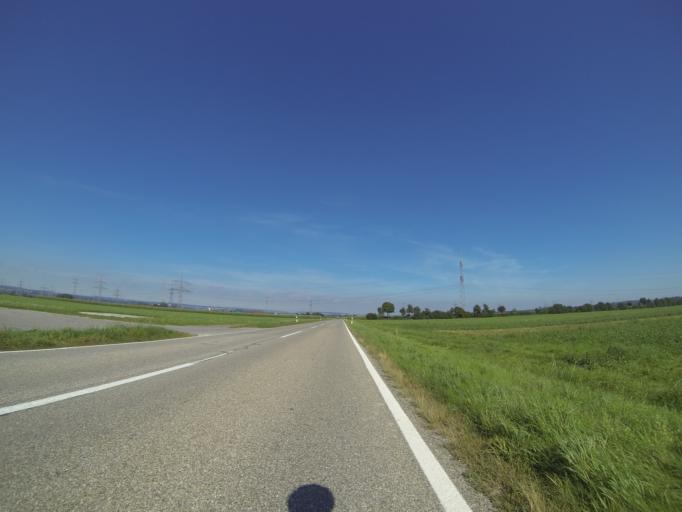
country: DE
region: Baden-Wuerttemberg
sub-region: Tuebingen Region
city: Achstetten
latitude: 48.2887
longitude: 9.9052
